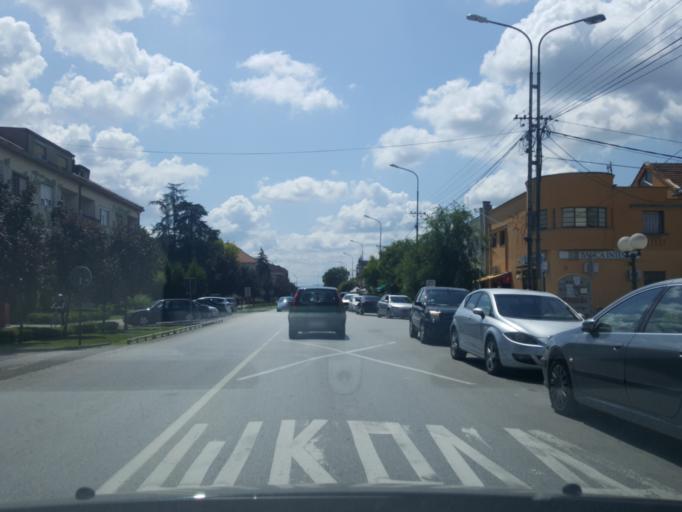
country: RS
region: Central Serbia
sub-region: Macvanski Okrug
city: Bogatic
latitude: 44.8367
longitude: 19.4802
